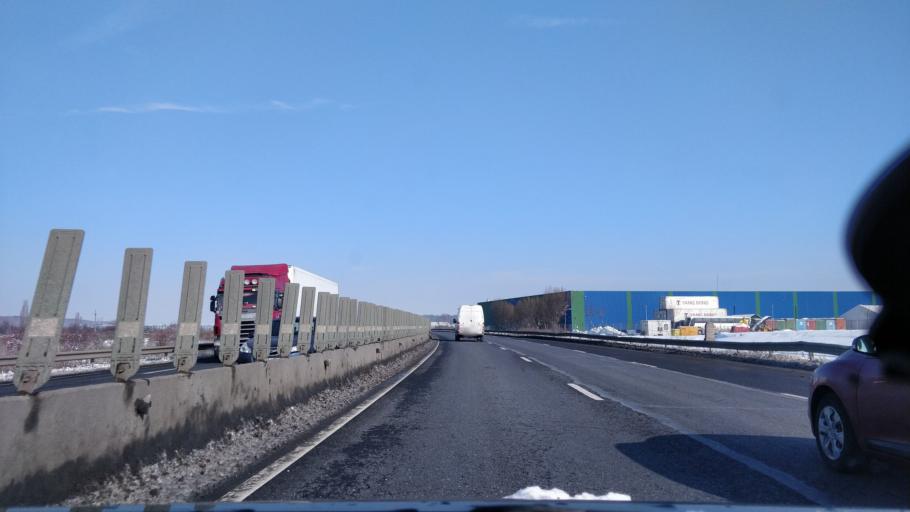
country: RO
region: Ilfov
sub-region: Comuna Chitila
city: Chitila
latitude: 44.5017
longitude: 26.0020
